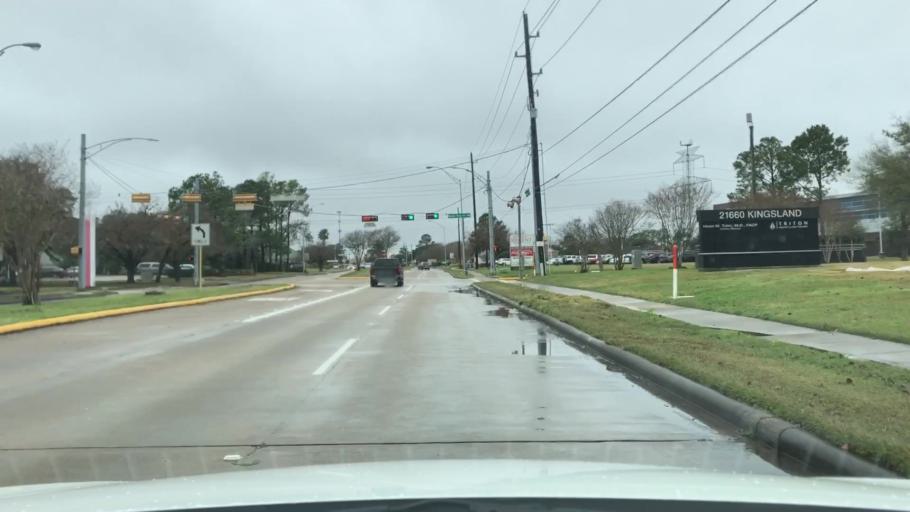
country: US
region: Texas
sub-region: Fort Bend County
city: Cinco Ranch
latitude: 29.7750
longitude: -95.7443
